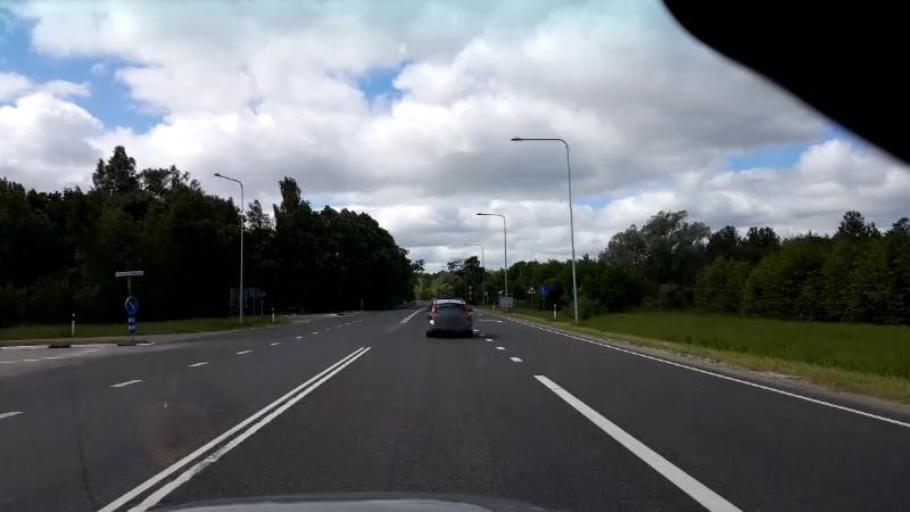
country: EE
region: Paernumaa
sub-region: Sauga vald
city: Sauga
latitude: 58.4458
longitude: 24.4981
